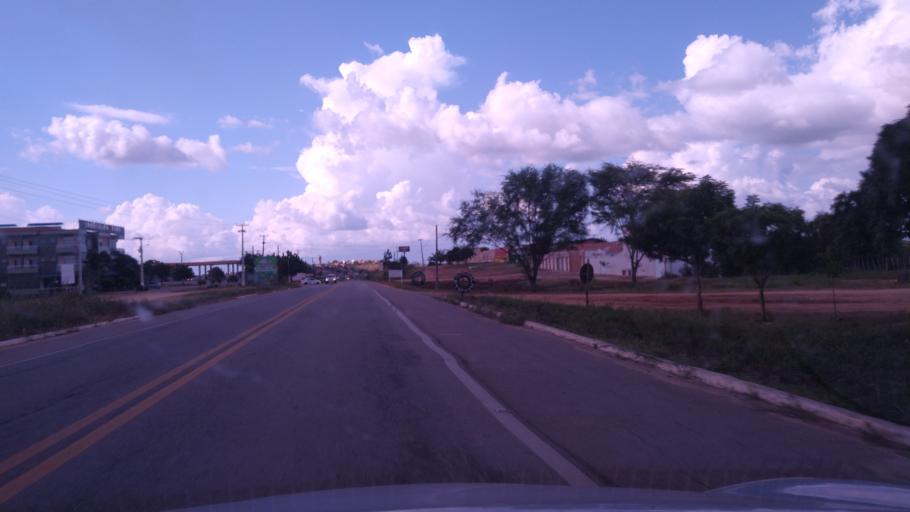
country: BR
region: Ceara
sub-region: Caninde
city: Caninde
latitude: -4.3843
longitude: -39.3116
